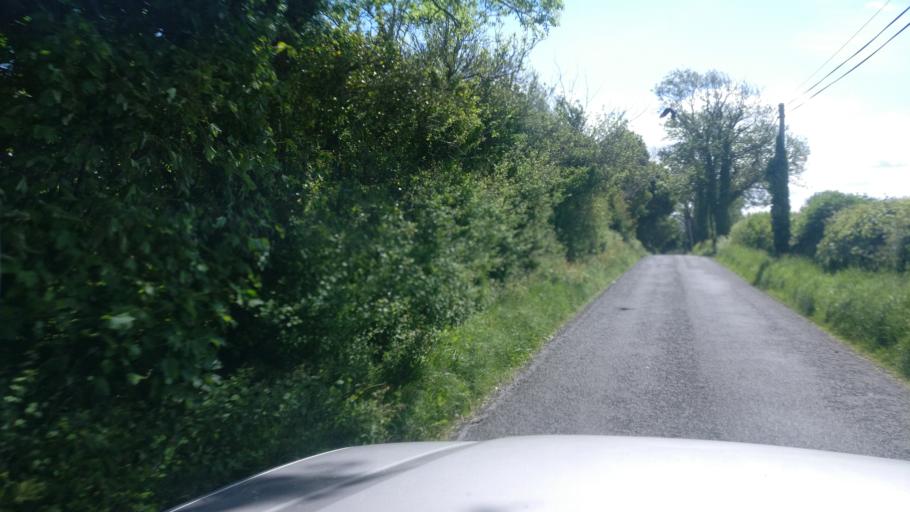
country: IE
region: Connaught
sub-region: County Galway
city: Gort
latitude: 53.1516
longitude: -8.7489
